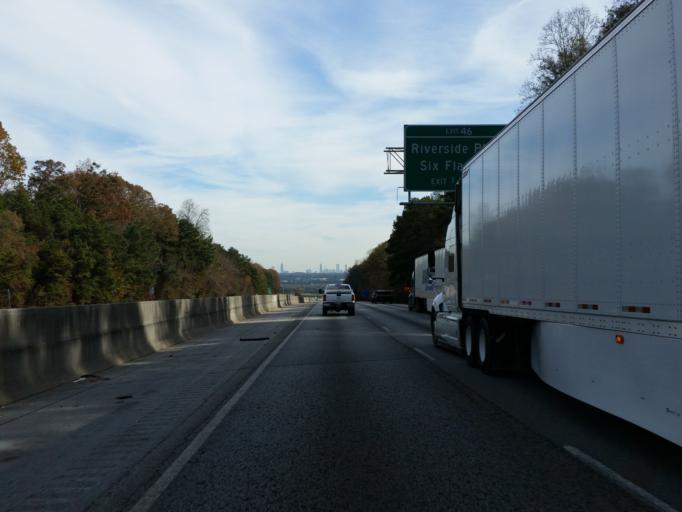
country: US
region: Georgia
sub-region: Cobb County
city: Mableton
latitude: 33.7746
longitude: -84.5724
